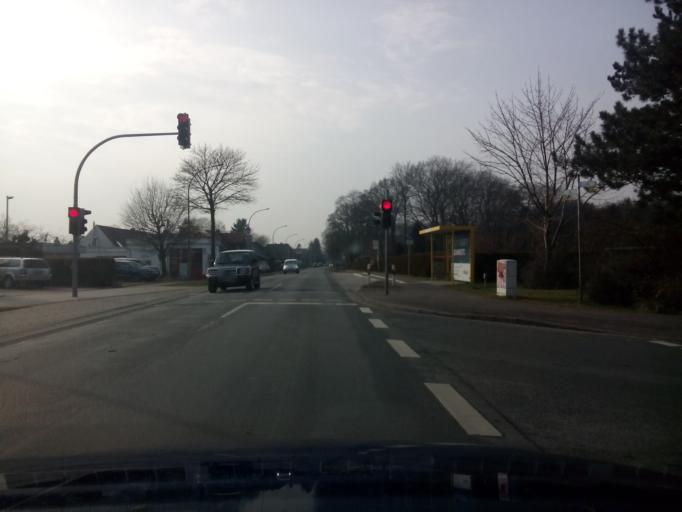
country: DE
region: Lower Saxony
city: Langen
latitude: 53.6112
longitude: 8.6100
